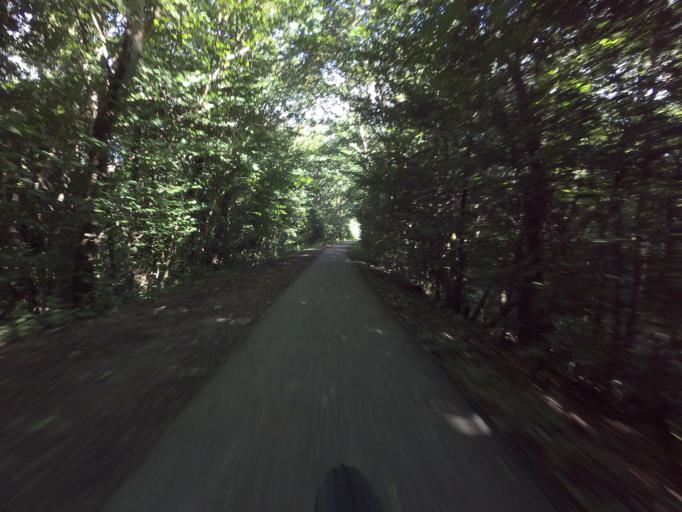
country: DK
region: Central Jutland
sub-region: Horsens Kommune
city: Braedstrup
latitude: 55.9711
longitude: 9.6902
